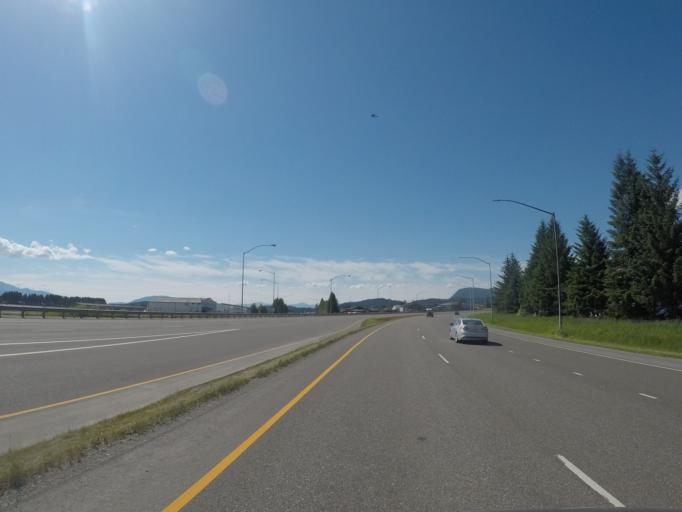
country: US
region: Alaska
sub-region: Juneau City and Borough
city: Juneau
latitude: 58.3584
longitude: -134.5619
